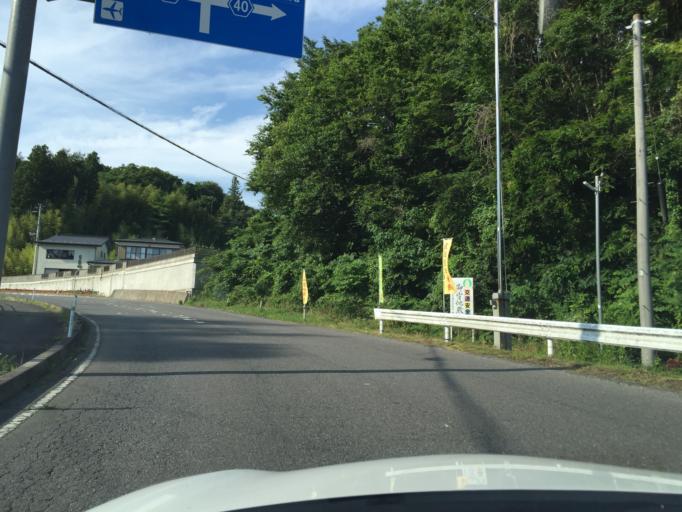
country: JP
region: Fukushima
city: Miharu
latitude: 37.3570
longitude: 140.5149
